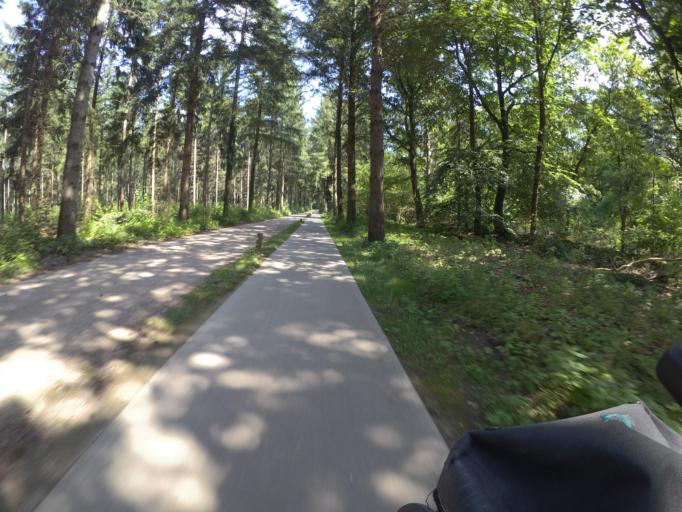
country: NL
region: Gelderland
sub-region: Gemeente Heerde
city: Heerde
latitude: 52.4251
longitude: 6.0574
